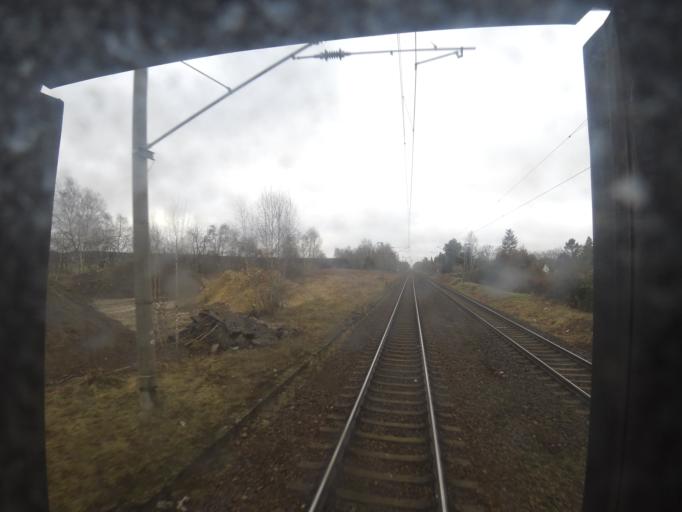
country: DE
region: Brandenburg
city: Rangsdorf
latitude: 52.3248
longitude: 13.4204
